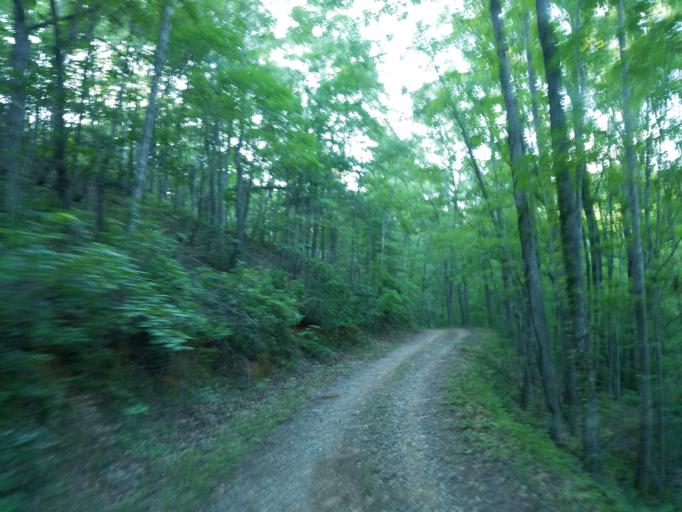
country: US
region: Georgia
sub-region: Fannin County
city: Blue Ridge
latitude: 34.8142
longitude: -84.1501
